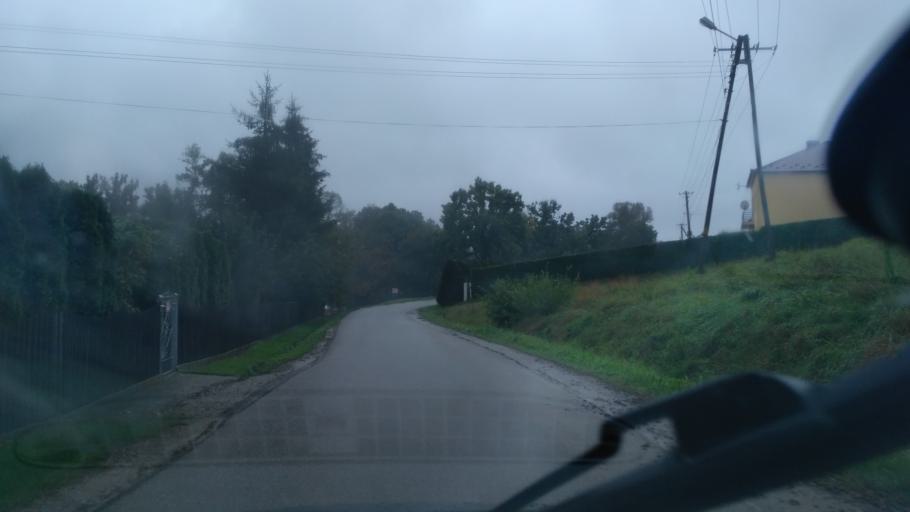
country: PL
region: Subcarpathian Voivodeship
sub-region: Powiat ropczycko-sedziszowski
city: Niedzwiada
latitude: 50.0242
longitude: 21.5407
